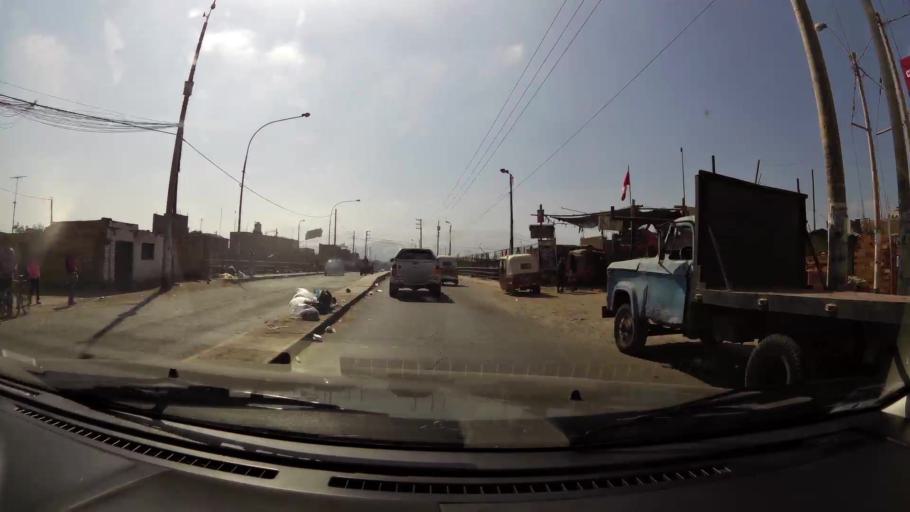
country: PE
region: Ica
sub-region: Provincia de Ica
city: Ica
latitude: -14.0706
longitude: -75.7210
